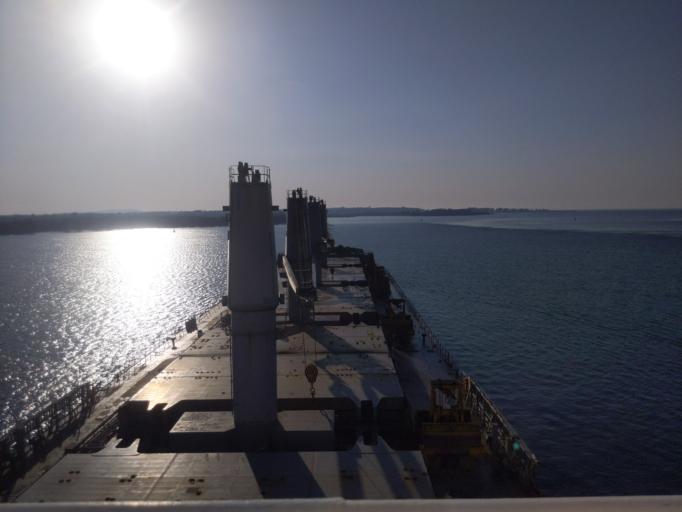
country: ZA
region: KwaZulu-Natal
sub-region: uThungulu District Municipality
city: Richards Bay
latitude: -28.8013
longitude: 32.0564
